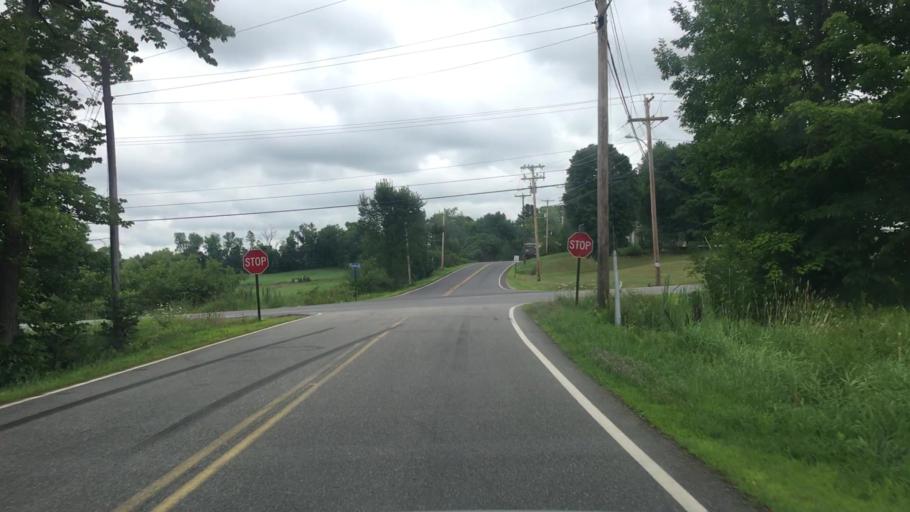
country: US
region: Maine
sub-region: York County
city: Dayton
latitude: 43.5369
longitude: -70.5121
